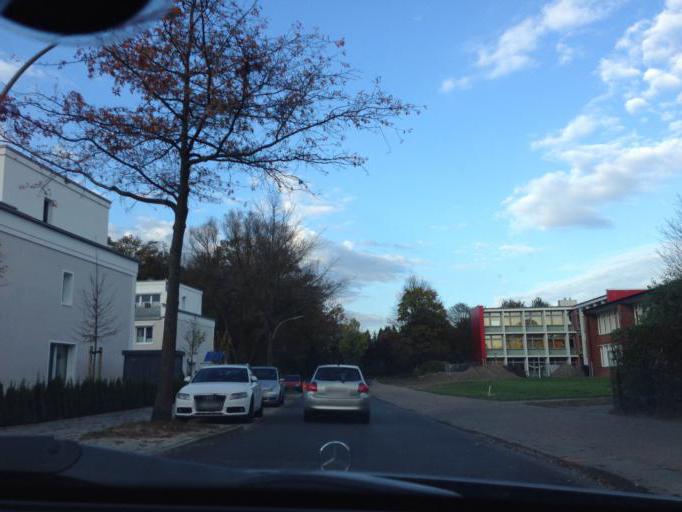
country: DE
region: Schleswig-Holstein
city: Barsbuettel
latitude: 53.5998
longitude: 10.1778
